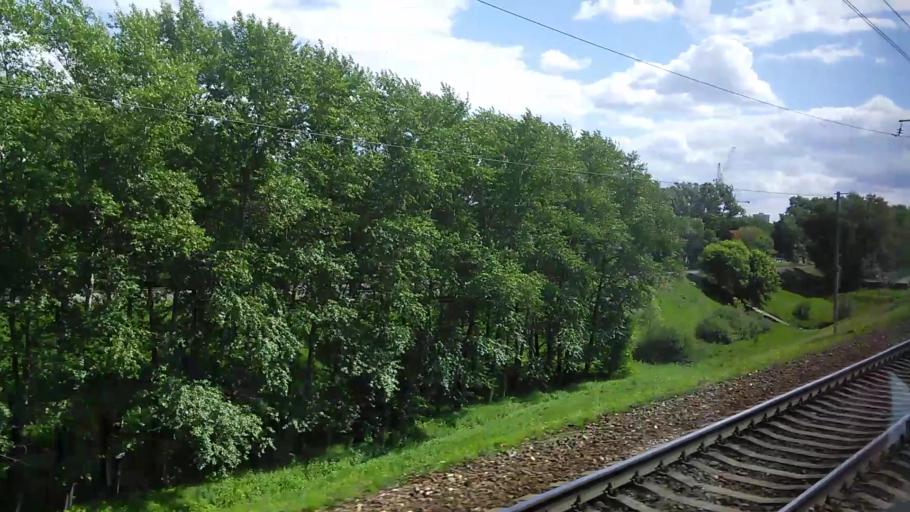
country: RU
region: Moscow
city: Likhobory
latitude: 55.8541
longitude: 37.5728
